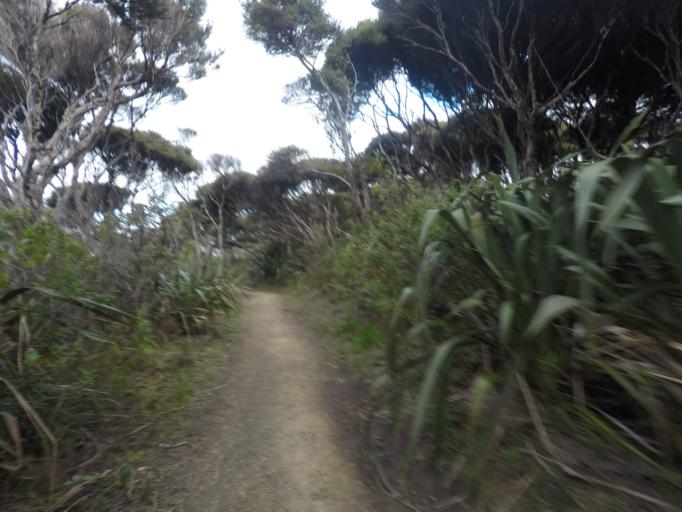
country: NZ
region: Auckland
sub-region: Auckland
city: Muriwai Beach
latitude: -36.9747
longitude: 174.4731
